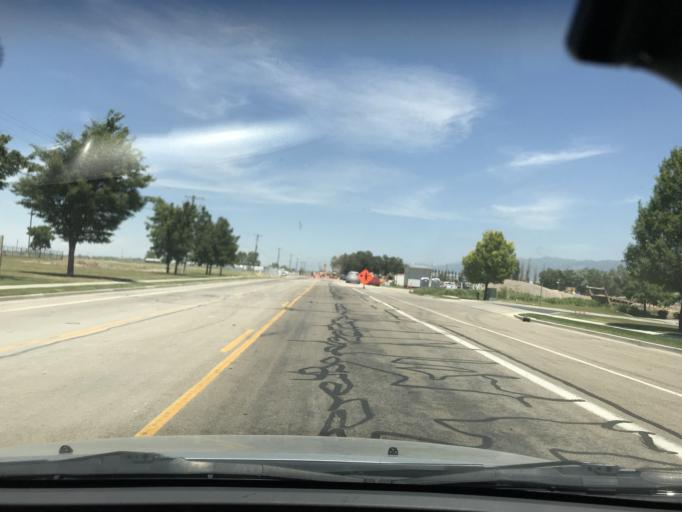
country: US
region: Utah
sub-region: Davis County
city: North Salt Lake
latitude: 40.8086
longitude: -111.9535
